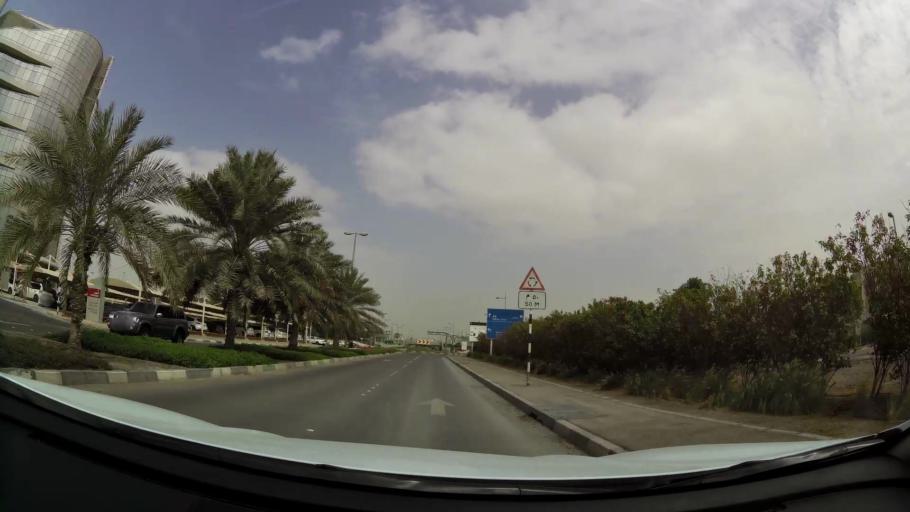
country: AE
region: Abu Dhabi
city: Abu Dhabi
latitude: 24.3963
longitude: 54.5019
